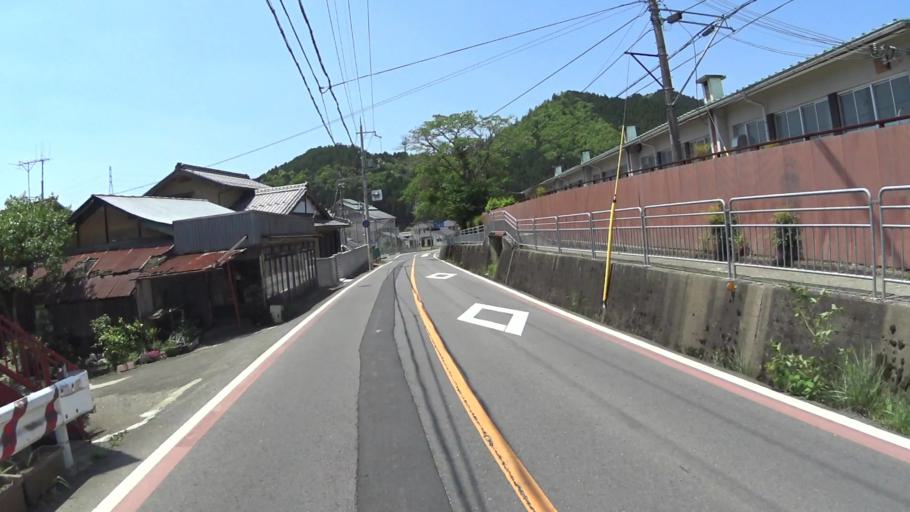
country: JP
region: Kyoto
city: Kameoka
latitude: 35.1567
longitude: 135.6358
